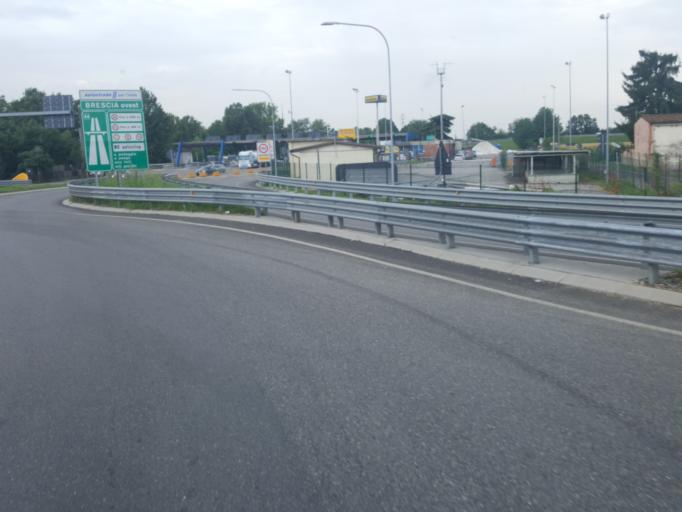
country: IT
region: Lombardy
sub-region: Provincia di Brescia
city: Roncadelle
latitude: 45.5291
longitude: 10.1684
